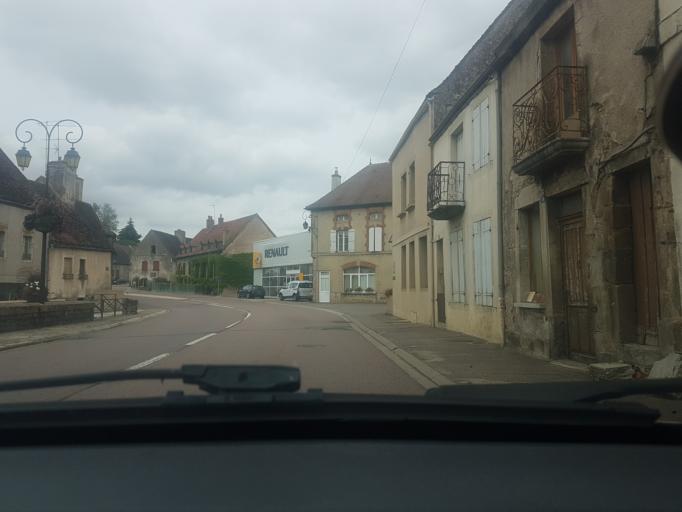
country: FR
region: Bourgogne
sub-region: Departement de la Cote-d'Or
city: Arnay-le-Duc
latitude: 47.1357
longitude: 4.4855
